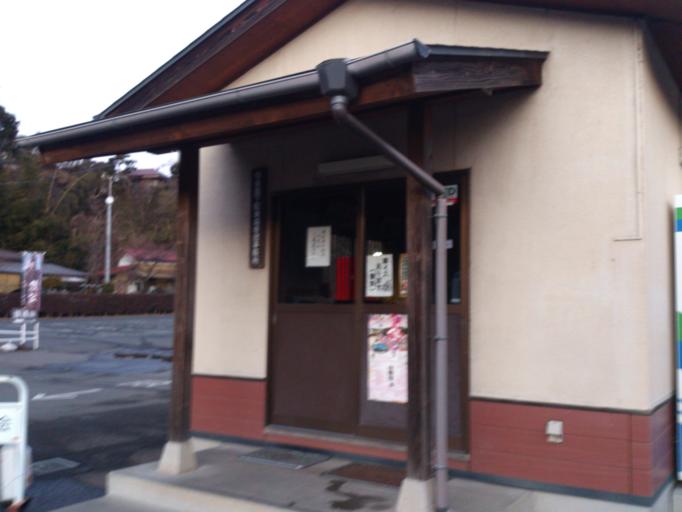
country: JP
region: Ibaraki
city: Mito-shi
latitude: 36.3734
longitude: 140.4562
